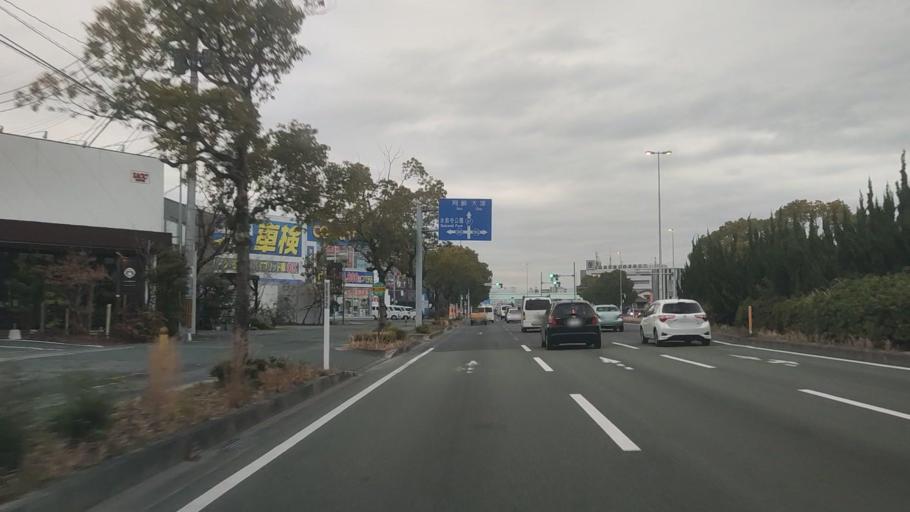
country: JP
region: Kumamoto
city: Kumamoto
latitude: 32.7733
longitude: 130.7338
